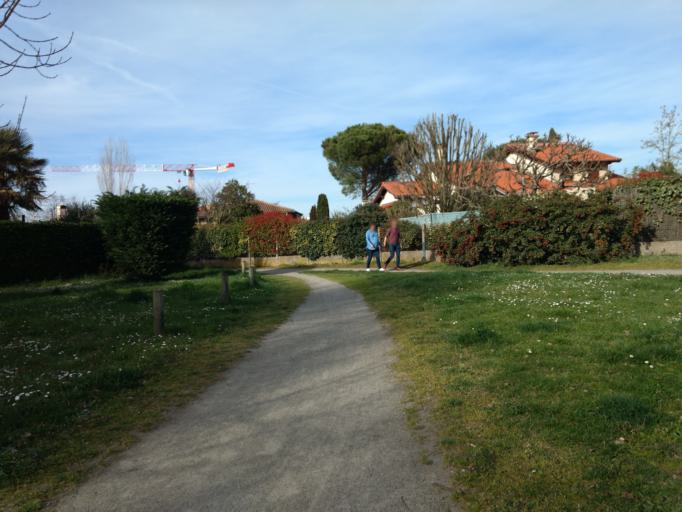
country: FR
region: Midi-Pyrenees
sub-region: Departement de la Haute-Garonne
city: Colomiers
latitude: 43.5847
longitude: 1.3544
